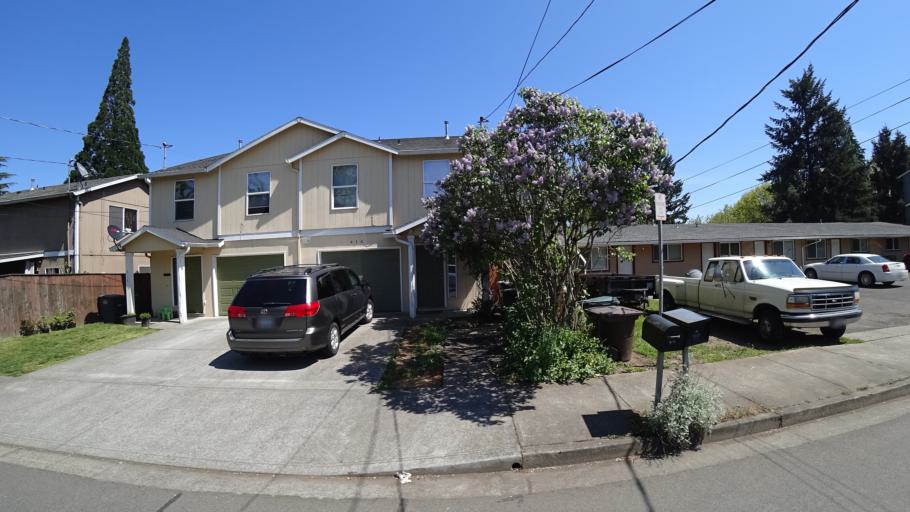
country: US
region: Oregon
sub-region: Washington County
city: Hillsboro
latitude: 45.5183
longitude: -122.9665
